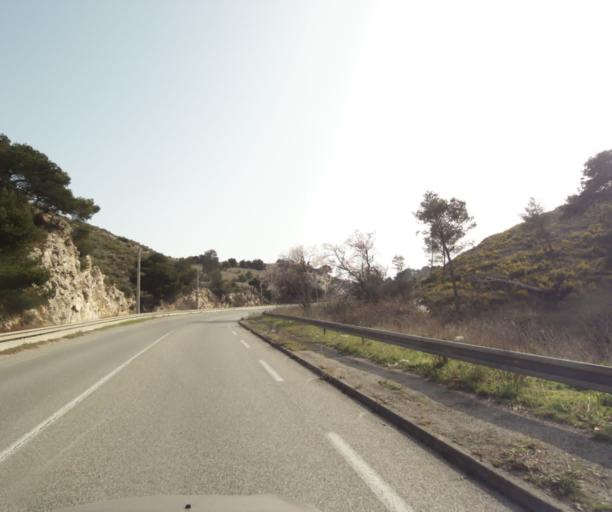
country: FR
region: Provence-Alpes-Cote d'Azur
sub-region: Departement des Bouches-du-Rhone
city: Les Pennes-Mirabeau
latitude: 43.4056
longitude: 5.3316
